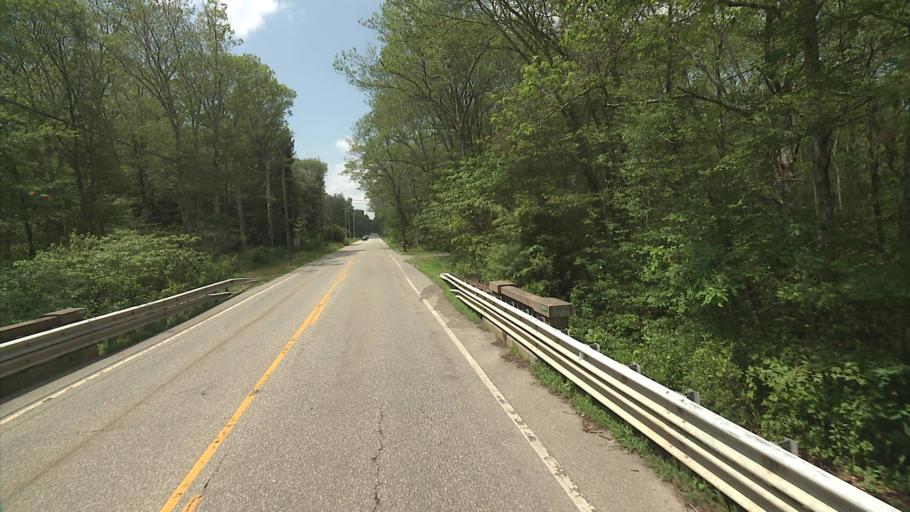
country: US
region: Rhode Island
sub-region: Washington County
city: Hope Valley
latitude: 41.5736
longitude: -71.7985
